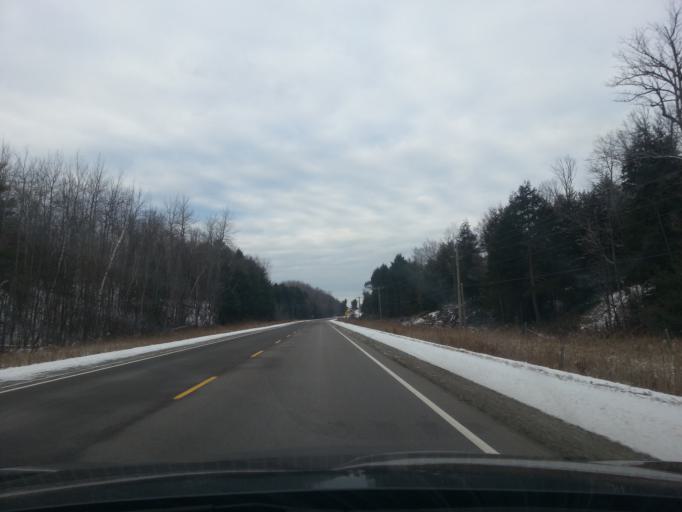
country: CA
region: Ontario
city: Skatepark
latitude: 44.7348
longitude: -76.9475
